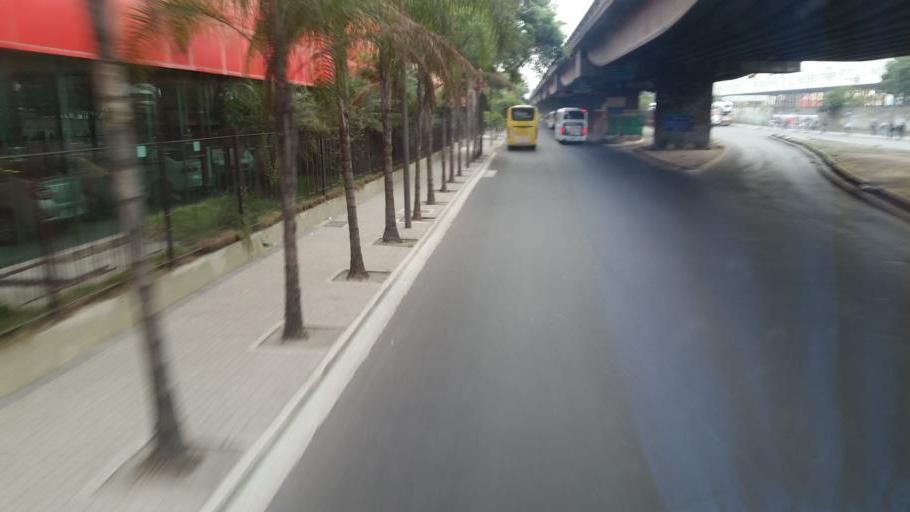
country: BR
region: Rio de Janeiro
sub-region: Rio De Janeiro
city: Rio de Janeiro
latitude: -22.8938
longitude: -43.2142
